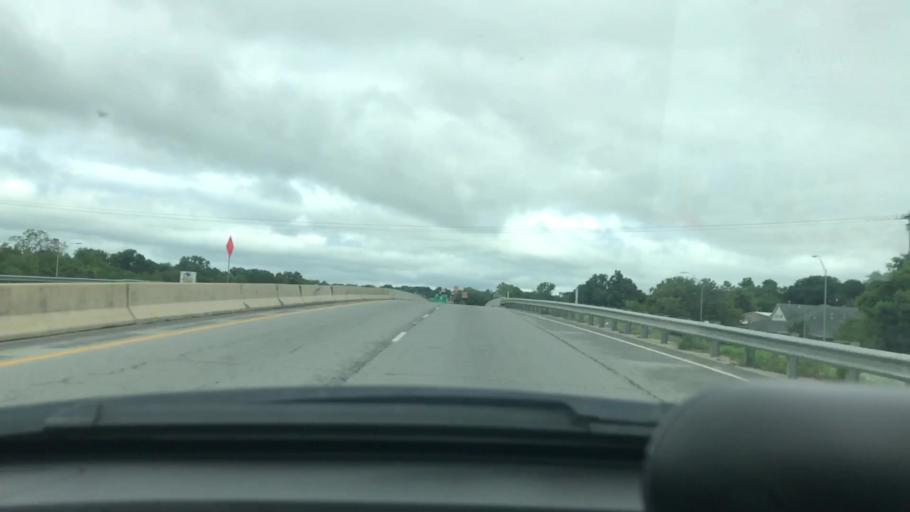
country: US
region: Texas
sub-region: Grayson County
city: Sherman
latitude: 33.6277
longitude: -96.6132
